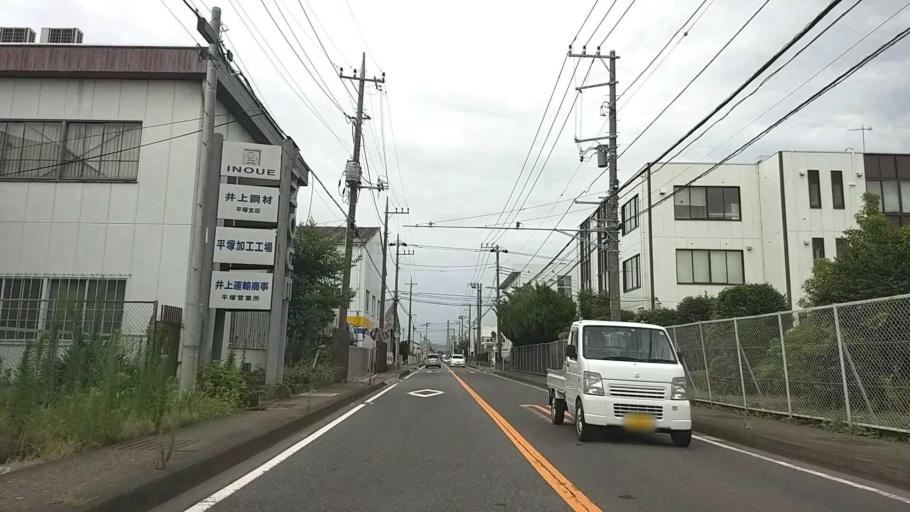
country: JP
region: Kanagawa
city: Isehara
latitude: 35.3760
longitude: 139.3599
